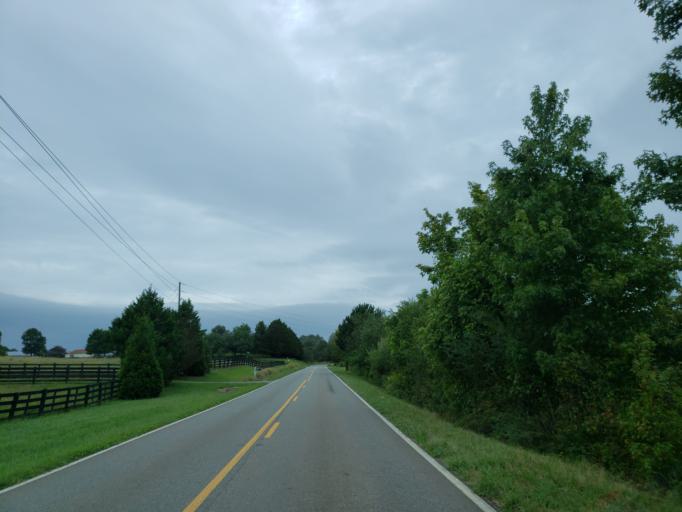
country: US
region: Georgia
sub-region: Pickens County
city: Jasper
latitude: 34.4395
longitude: -84.5832
